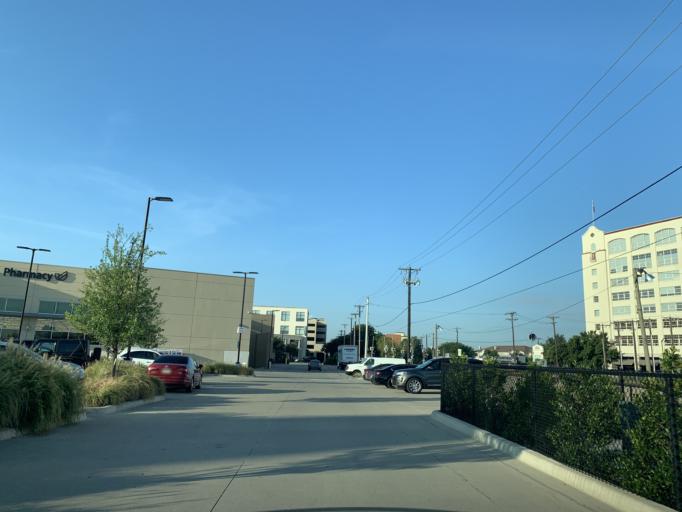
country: US
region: Texas
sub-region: Tarrant County
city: Fort Worth
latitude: 32.7523
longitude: -97.3515
